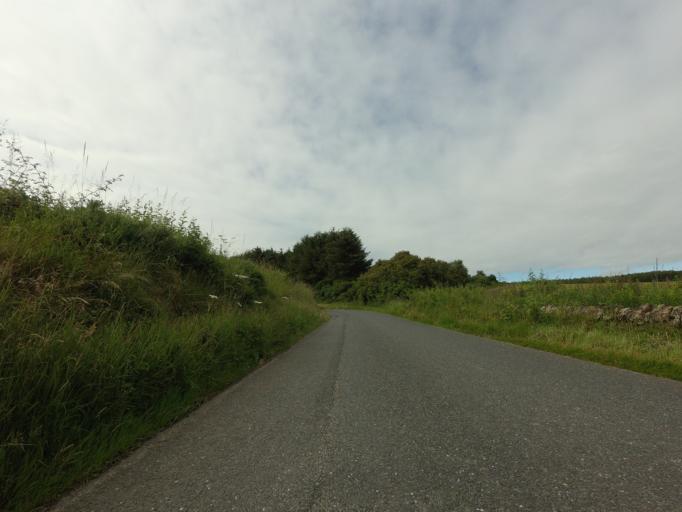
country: GB
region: Scotland
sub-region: Aberdeenshire
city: Turriff
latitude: 57.5328
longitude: -2.4012
